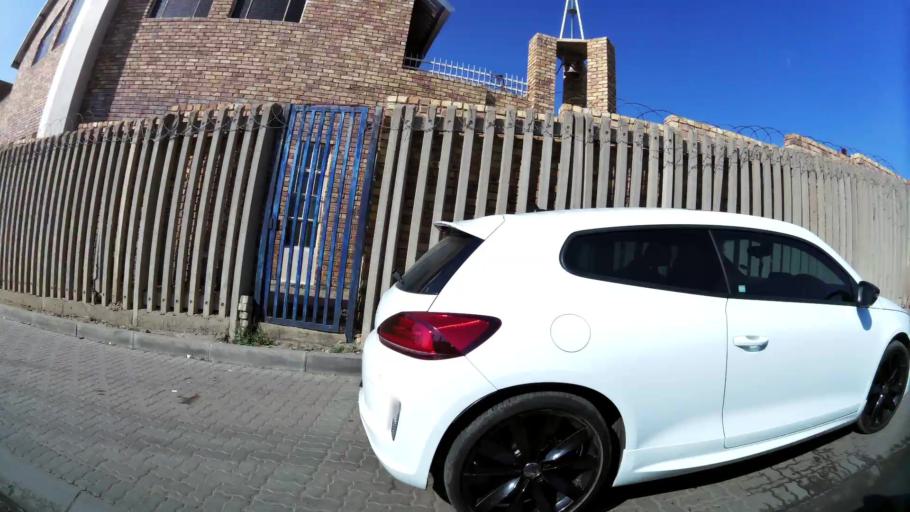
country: ZA
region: Gauteng
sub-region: City of Johannesburg Metropolitan Municipality
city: Modderfontein
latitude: -26.1079
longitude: 28.0918
